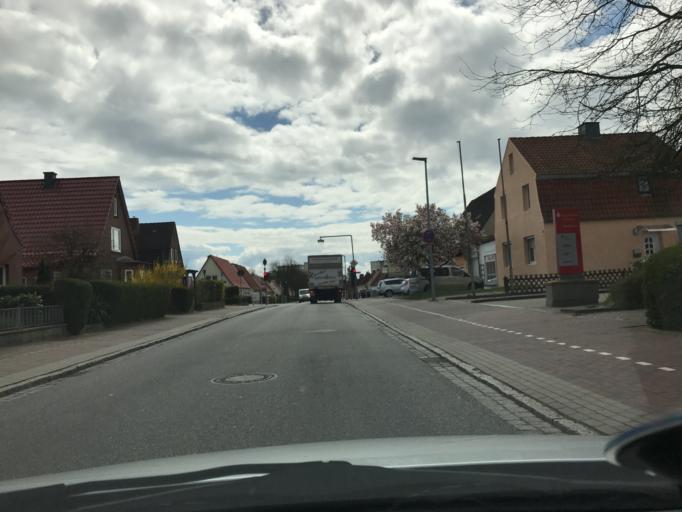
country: DE
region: Schleswig-Holstein
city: Neustadt in Holstein
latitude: 54.1017
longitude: 10.8212
